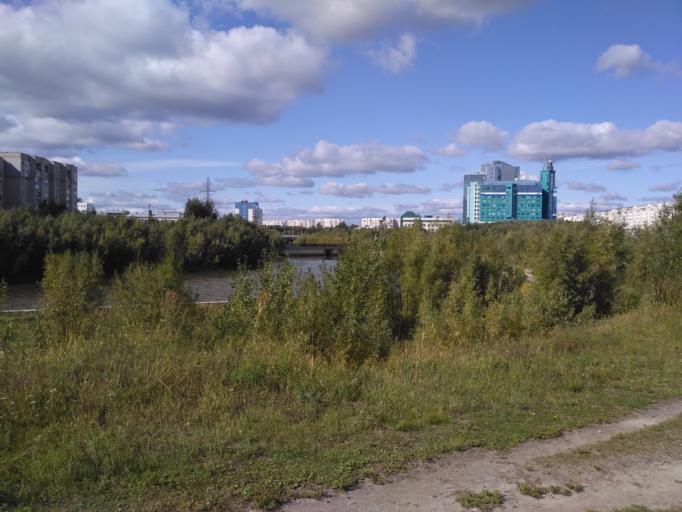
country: RU
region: Khanty-Mansiyskiy Avtonomnyy Okrug
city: Surgut
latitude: 61.2408
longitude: 73.4073
